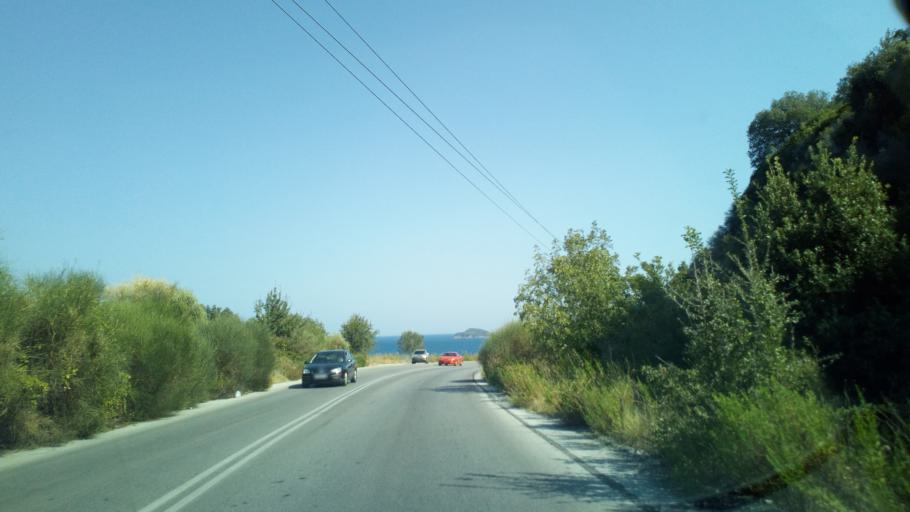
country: GR
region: Central Macedonia
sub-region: Nomos Thessalonikis
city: Stavros
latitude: 40.6327
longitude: 23.7607
